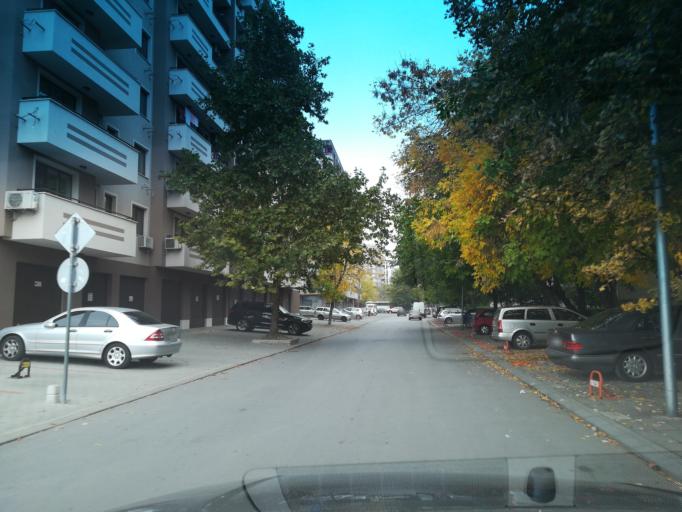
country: BG
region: Plovdiv
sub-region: Obshtina Plovdiv
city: Plovdiv
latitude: 42.1373
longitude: 24.7932
